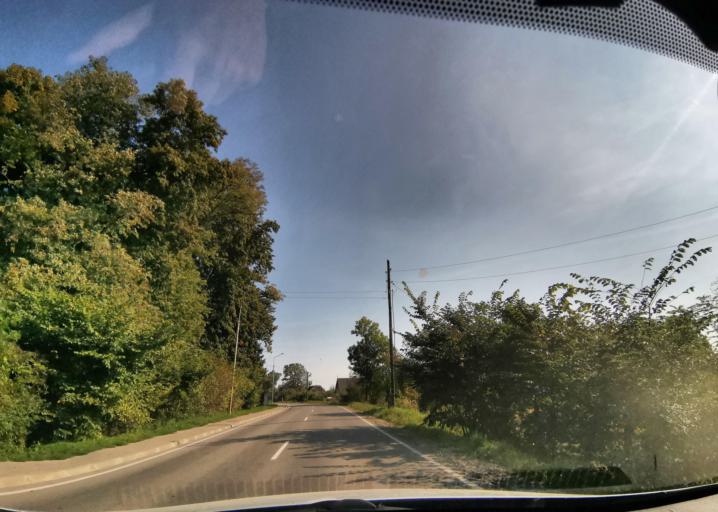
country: RU
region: Kaliningrad
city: Neman
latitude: 55.0305
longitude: 22.0465
